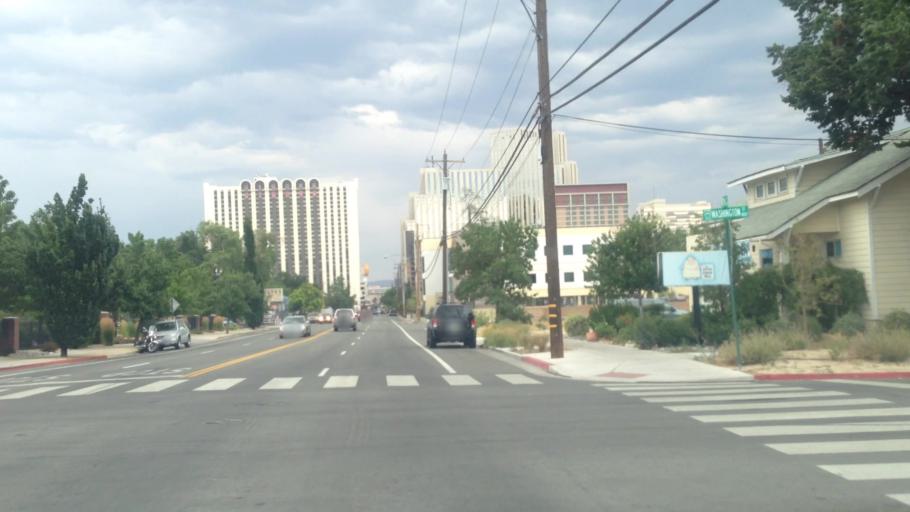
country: US
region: Nevada
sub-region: Washoe County
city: Reno
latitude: 39.5294
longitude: -119.8240
